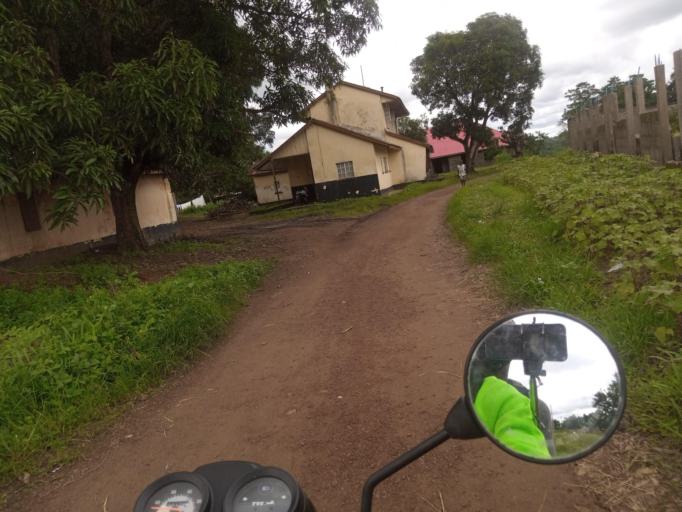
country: SL
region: Northern Province
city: Port Loko
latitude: 8.7659
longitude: -12.7769
